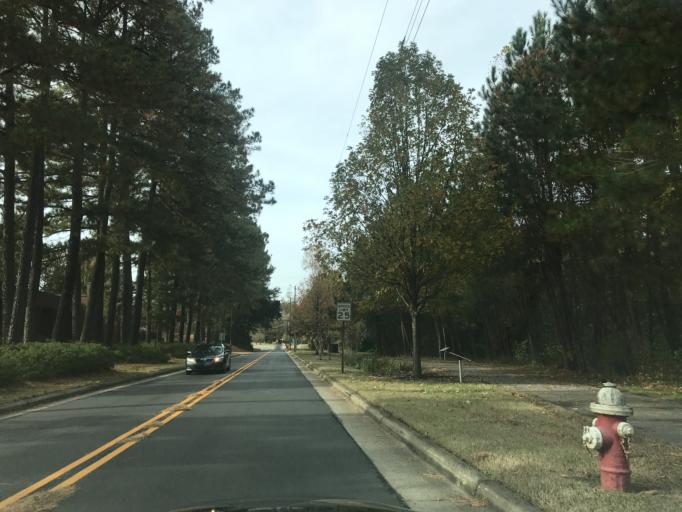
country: US
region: North Carolina
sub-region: Wake County
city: West Raleigh
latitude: 35.7875
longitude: -78.6823
